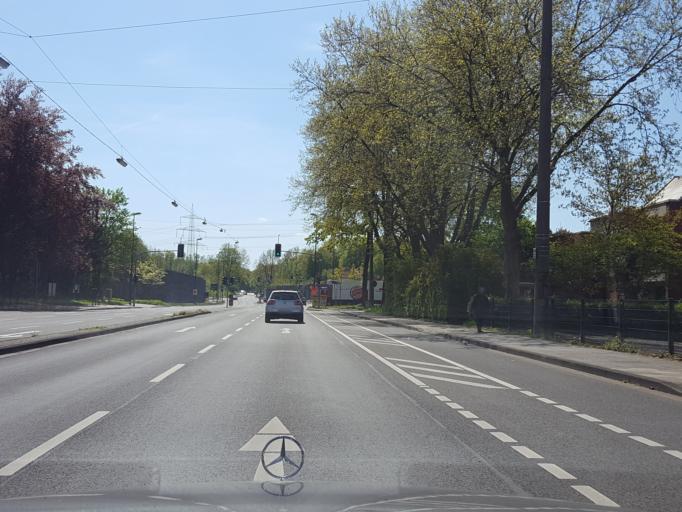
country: DE
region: North Rhine-Westphalia
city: Castrop-Rauxel
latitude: 51.5835
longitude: 7.3101
